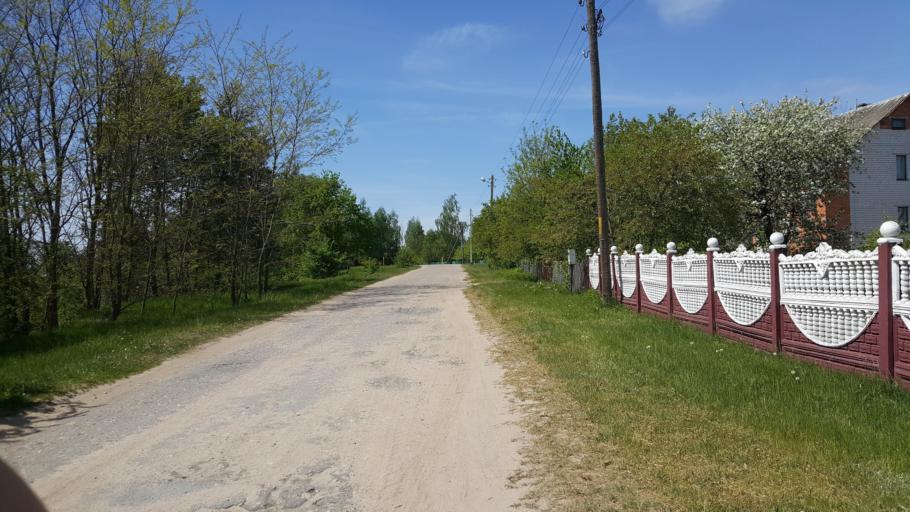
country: BY
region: Brest
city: Kobryn
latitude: 52.3383
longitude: 24.2557
